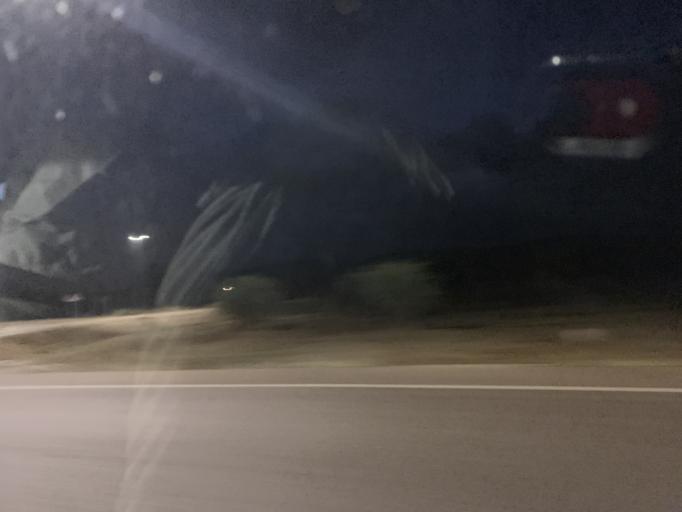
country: ES
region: Extremadura
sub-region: Provincia de Badajoz
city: Badajoz
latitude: 38.8849
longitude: -6.9298
